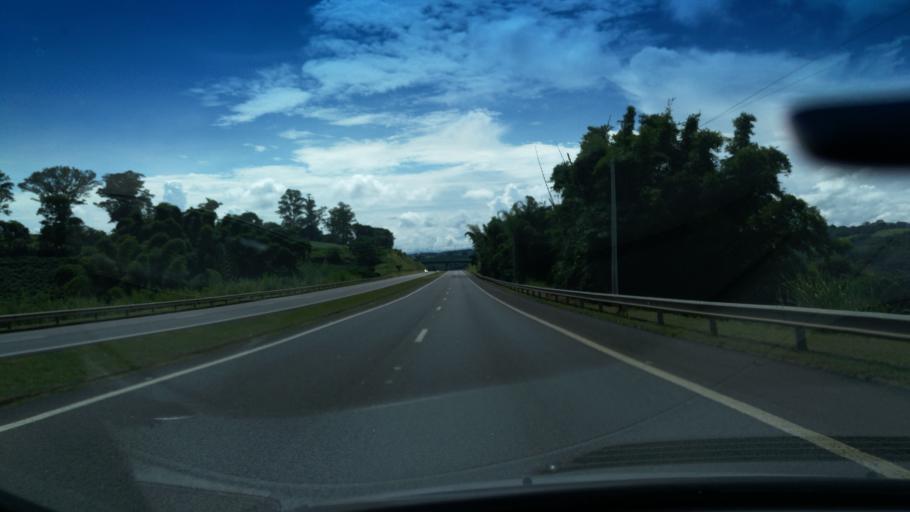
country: BR
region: Sao Paulo
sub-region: Santo Antonio Do Jardim
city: Espirito Santo do Pinhal
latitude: -22.2441
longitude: -46.8052
